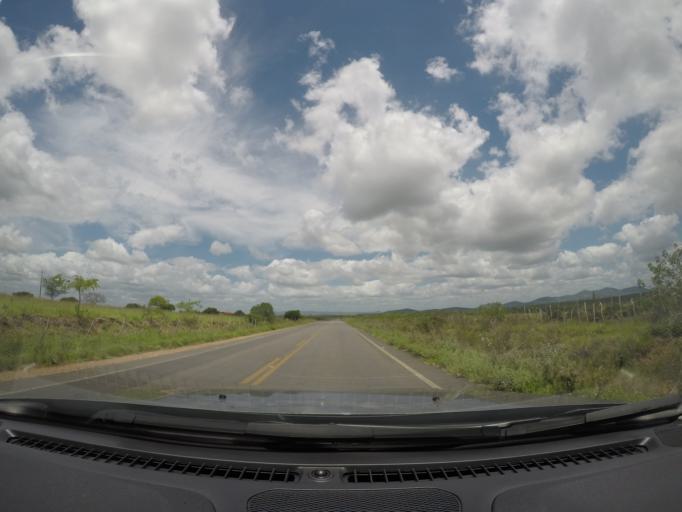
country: BR
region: Bahia
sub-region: Ipira
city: Ipira
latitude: -12.2948
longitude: -39.8847
